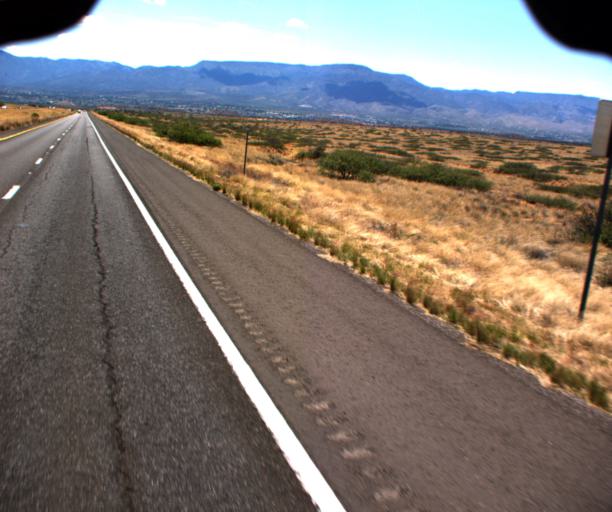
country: US
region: Arizona
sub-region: Yavapai County
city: Cornville
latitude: 34.7574
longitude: -111.9527
